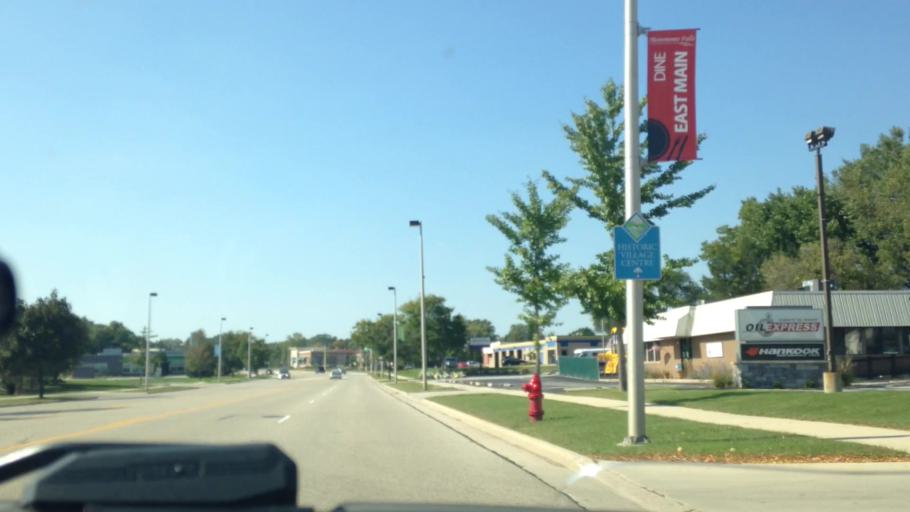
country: US
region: Wisconsin
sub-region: Waukesha County
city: Menomonee Falls
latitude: 43.1783
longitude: -88.0992
